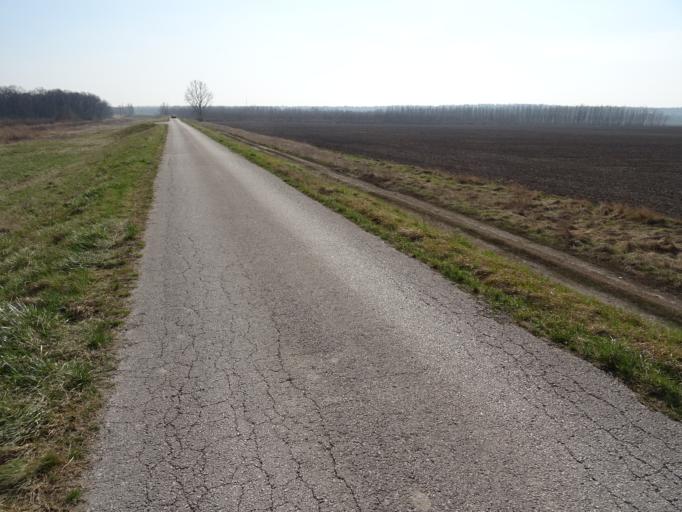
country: HU
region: Fejer
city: Racalmas
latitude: 47.0700
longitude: 18.9521
